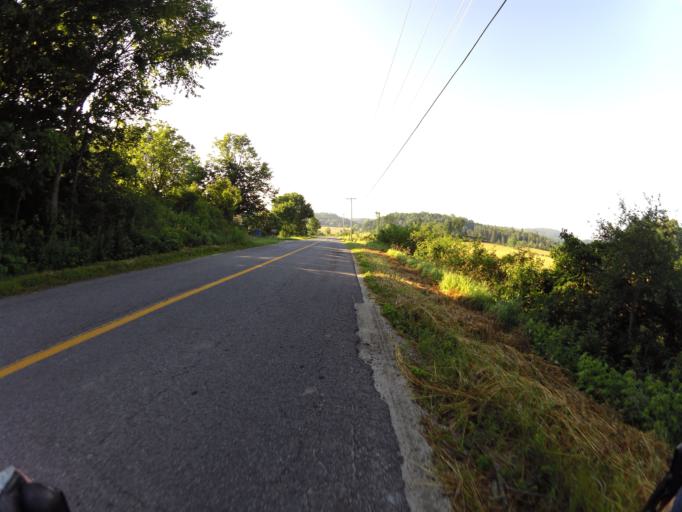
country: CA
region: Quebec
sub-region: Outaouais
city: Wakefield
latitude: 45.6992
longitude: -75.9587
